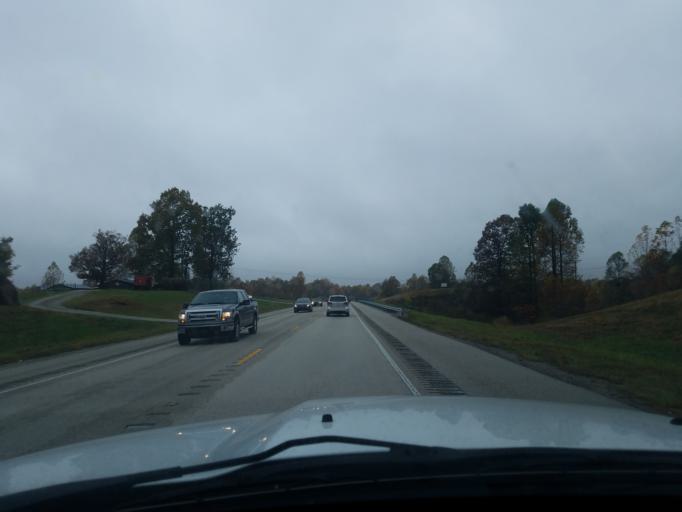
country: US
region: Kentucky
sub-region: Larue County
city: Hodgenville
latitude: 37.4647
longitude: -85.5722
